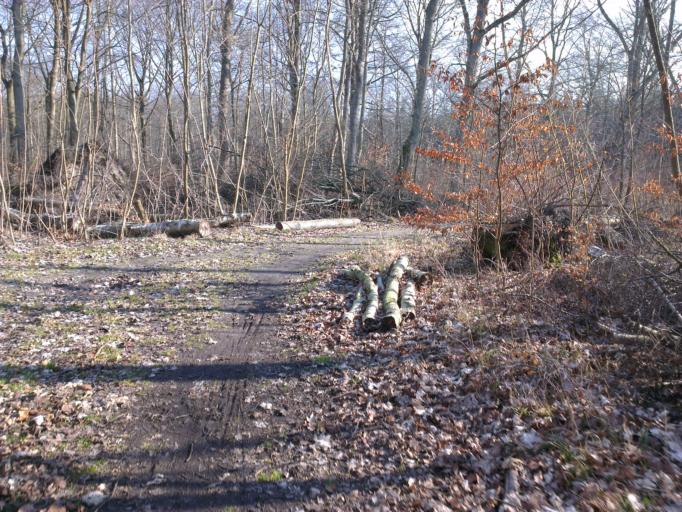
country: DK
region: Capital Region
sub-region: Frederikssund Kommune
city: Jaegerspris
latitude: 55.9113
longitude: 11.9827
